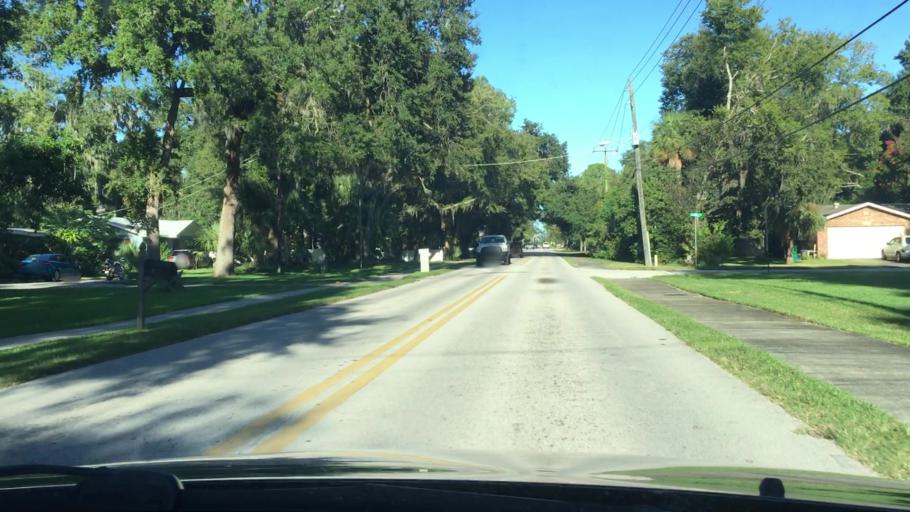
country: US
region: Florida
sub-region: Volusia County
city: Holly Hill
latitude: 29.2501
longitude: -81.0603
